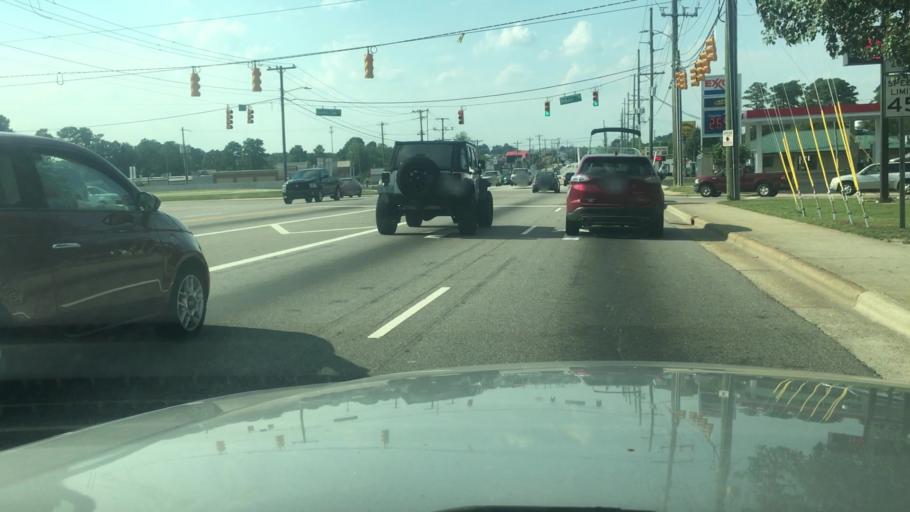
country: US
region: North Carolina
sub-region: Cumberland County
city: Fayetteville
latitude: 35.1047
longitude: -78.8783
